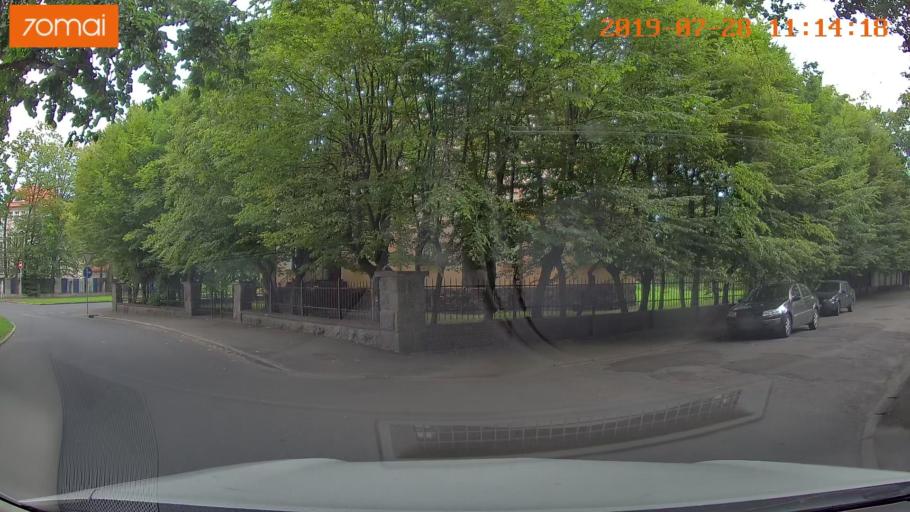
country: RU
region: Kaliningrad
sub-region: Gorod Kaliningrad
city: Kaliningrad
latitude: 54.7194
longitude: 20.4698
